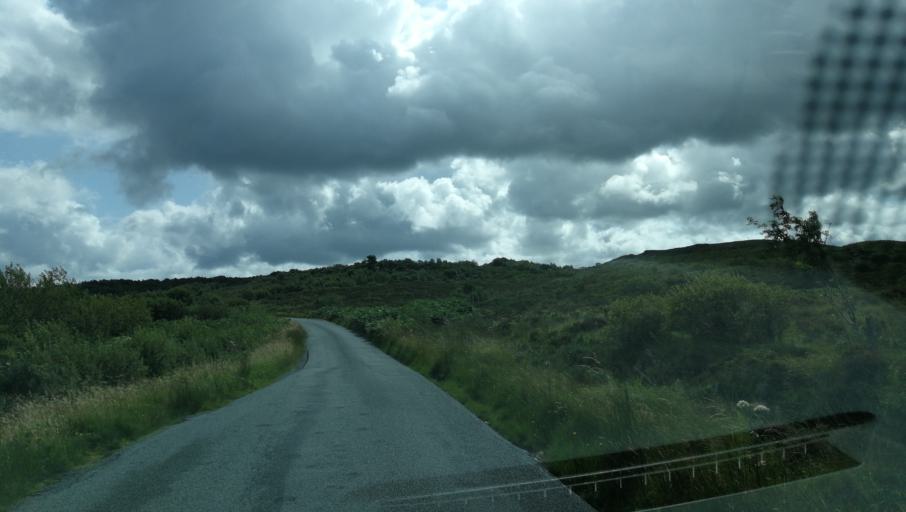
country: GB
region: Scotland
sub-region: Highland
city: Portree
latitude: 57.3844
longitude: -6.1858
